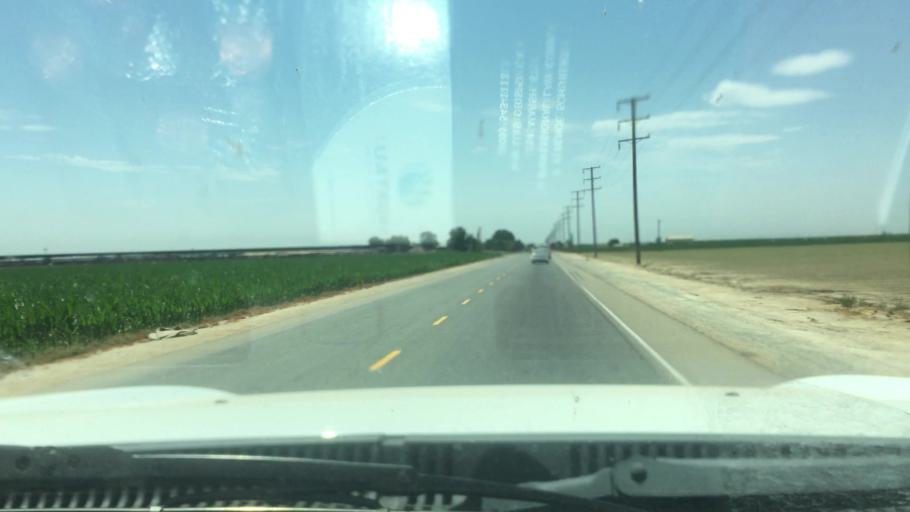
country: US
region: California
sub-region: Tulare County
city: Tipton
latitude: 36.0657
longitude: -119.2832
